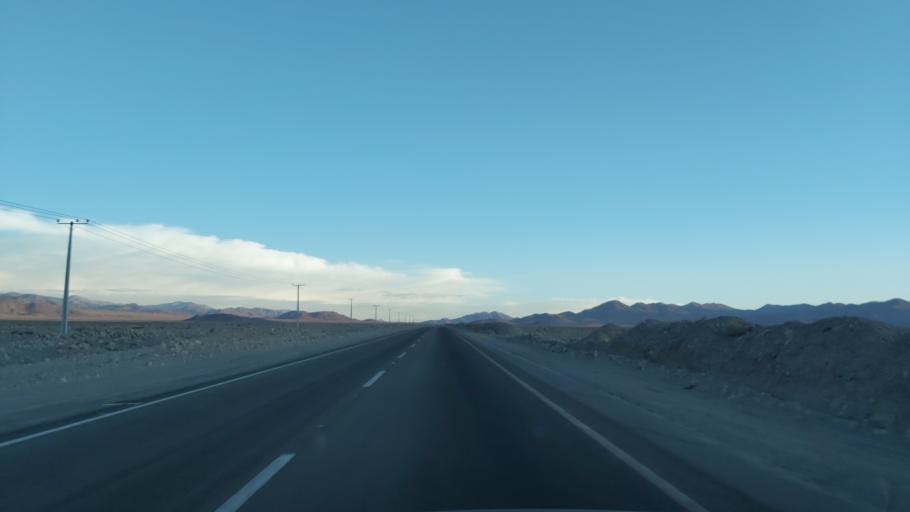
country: CL
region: Atacama
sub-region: Provincia de Chanaral
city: Diego de Almagro
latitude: -26.6875
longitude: -69.9321
